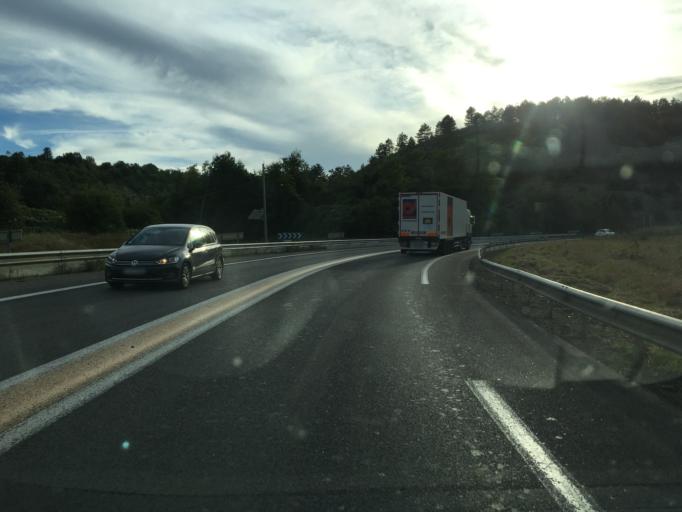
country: FR
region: Bourgogne
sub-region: Departement de la Cote-d'Or
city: Plombieres-les-Dijon
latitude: 47.3325
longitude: 4.9796
